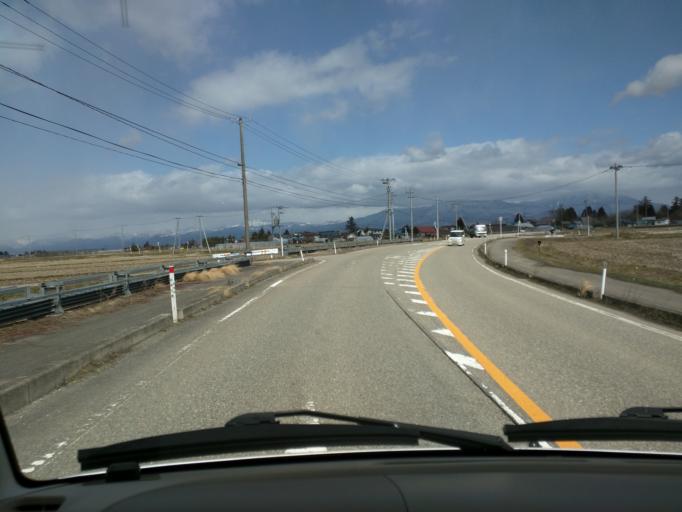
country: JP
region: Fukushima
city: Kitakata
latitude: 37.4915
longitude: 139.8545
